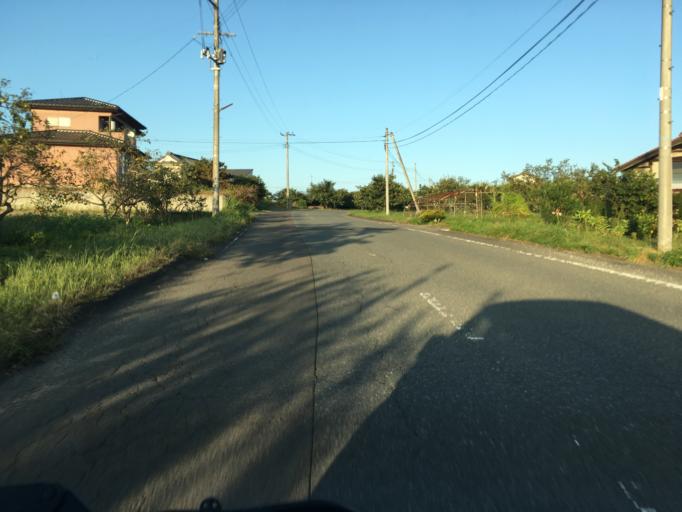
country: JP
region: Fukushima
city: Hobaramachi
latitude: 37.8035
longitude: 140.5692
